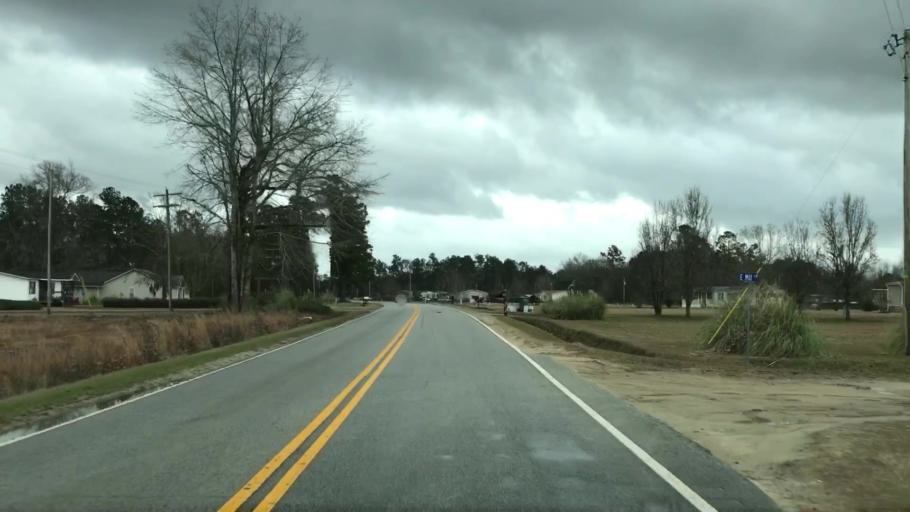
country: US
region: South Carolina
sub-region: Williamsburg County
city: Andrews
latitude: 33.4935
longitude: -79.5065
